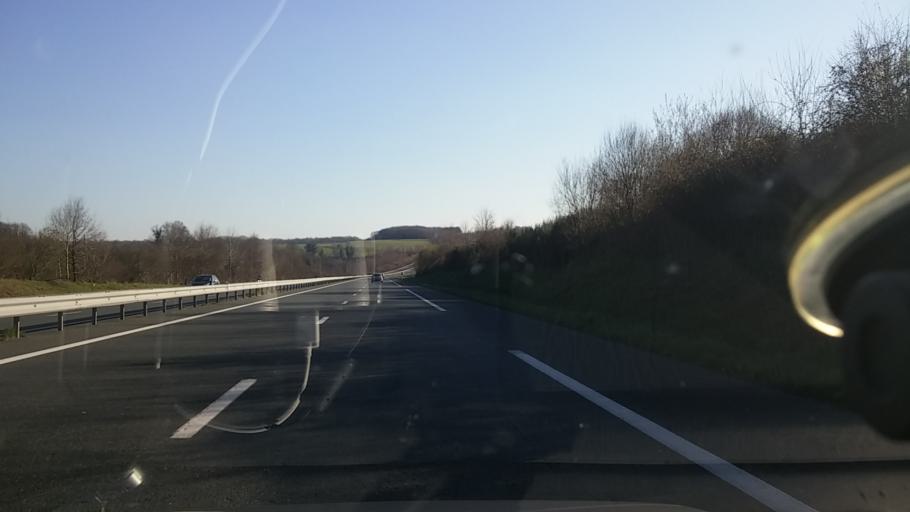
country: FR
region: Limousin
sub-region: Departement de la Haute-Vienne
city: Saint-Sulpice-les-Feuilles
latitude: 46.3851
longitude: 1.4488
